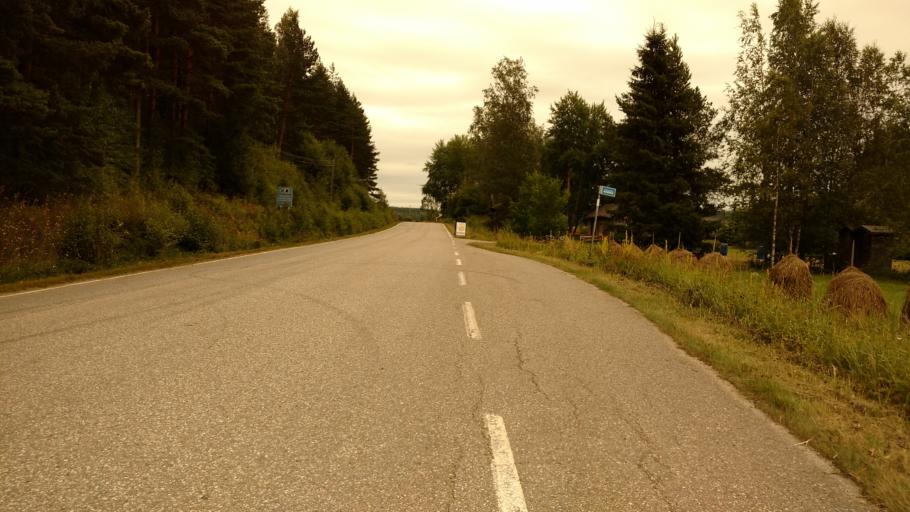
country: FI
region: Varsinais-Suomi
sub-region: Loimaa
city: Marttila
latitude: 60.4154
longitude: 22.8728
